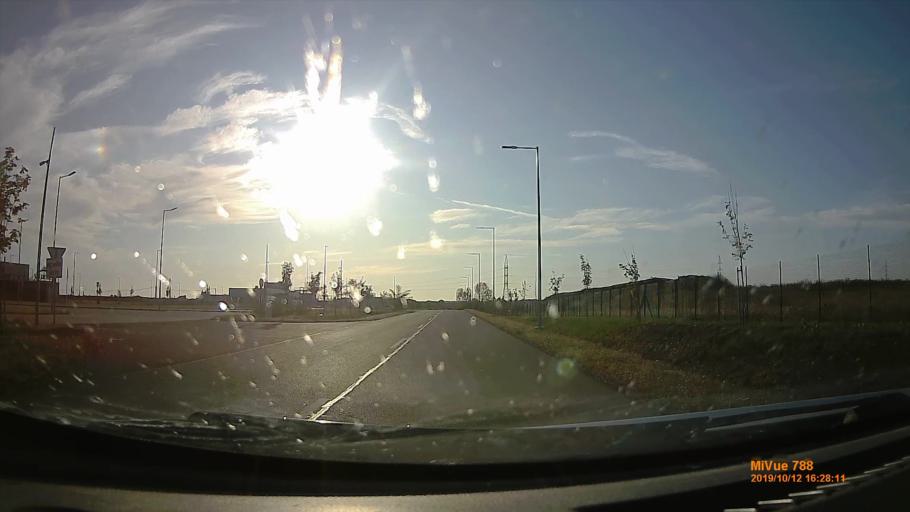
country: HU
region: Heves
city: Gyongyoshalasz
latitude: 47.7235
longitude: 19.9566
